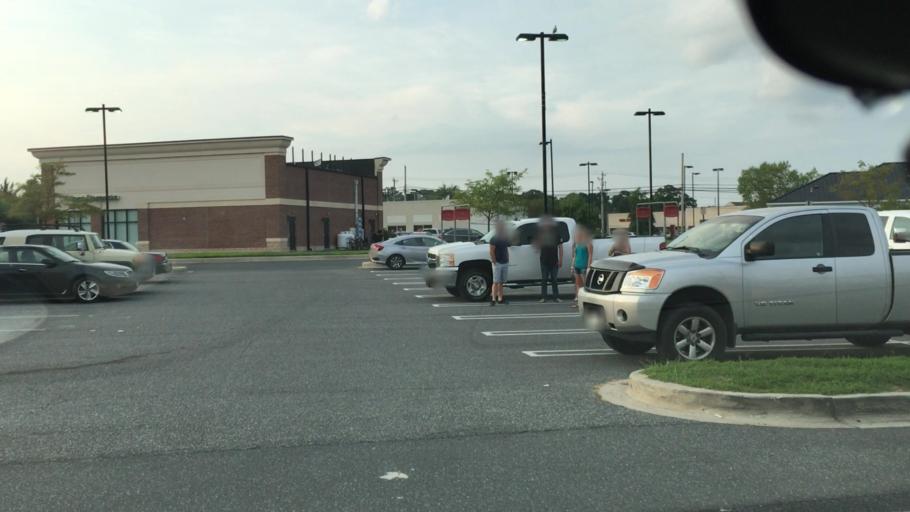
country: US
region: Delaware
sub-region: Sussex County
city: Ocean View
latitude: 38.5460
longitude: -75.1080
